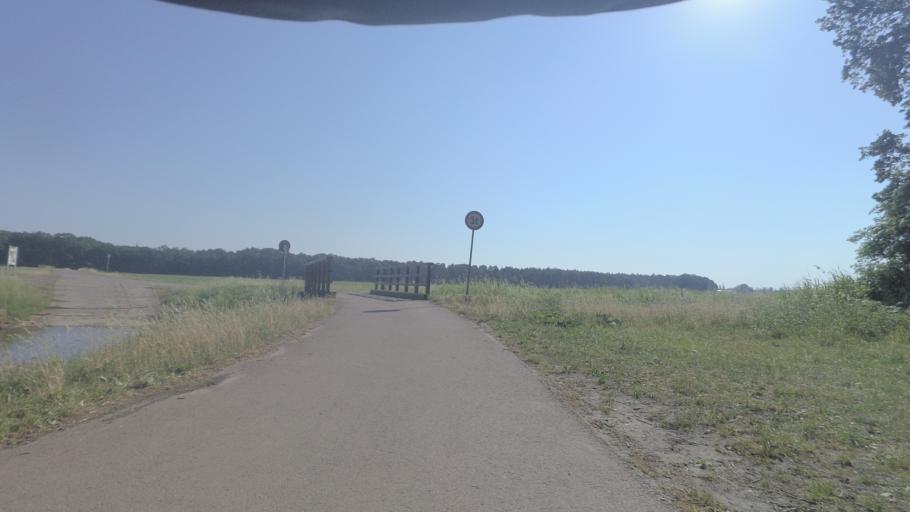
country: DE
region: Saxony-Anhalt
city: Quellendorf
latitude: 51.8235
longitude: 12.1602
